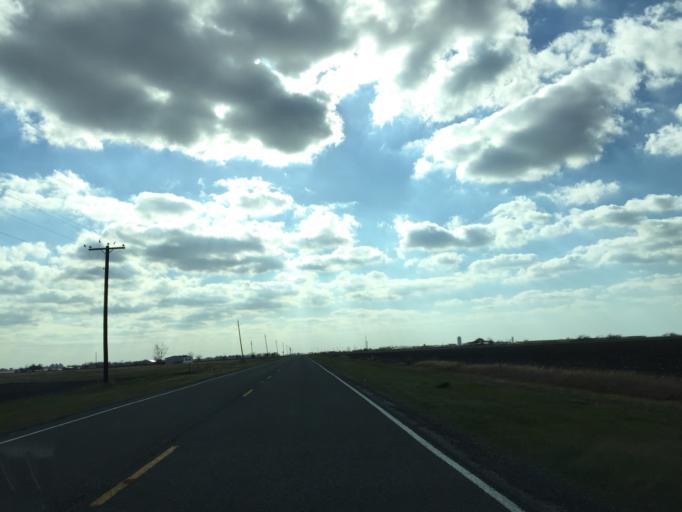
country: US
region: Texas
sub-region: Williamson County
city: Granger
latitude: 30.6599
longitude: -97.3719
